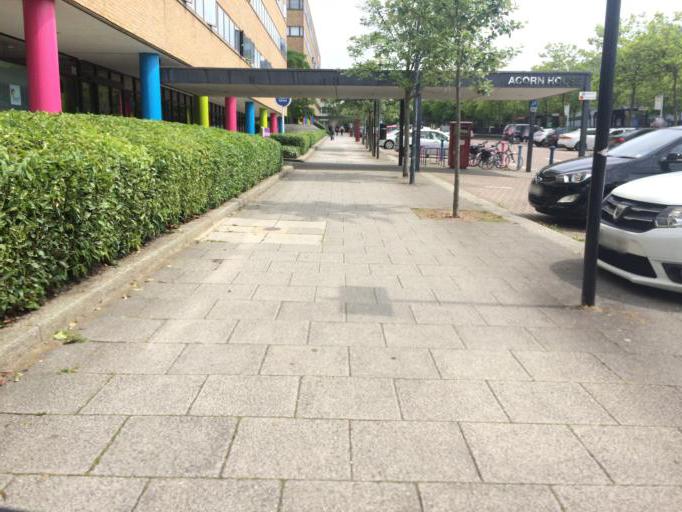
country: GB
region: England
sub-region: Milton Keynes
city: Milton Keynes
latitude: 52.0394
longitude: -0.7633
